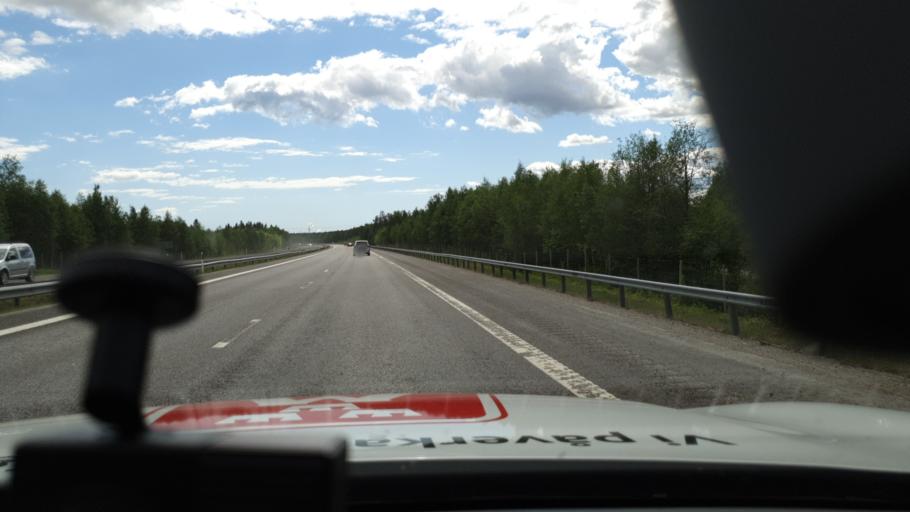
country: SE
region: Norrbotten
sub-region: Pitea Kommun
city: Norrfjarden
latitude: 65.3683
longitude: 21.4290
